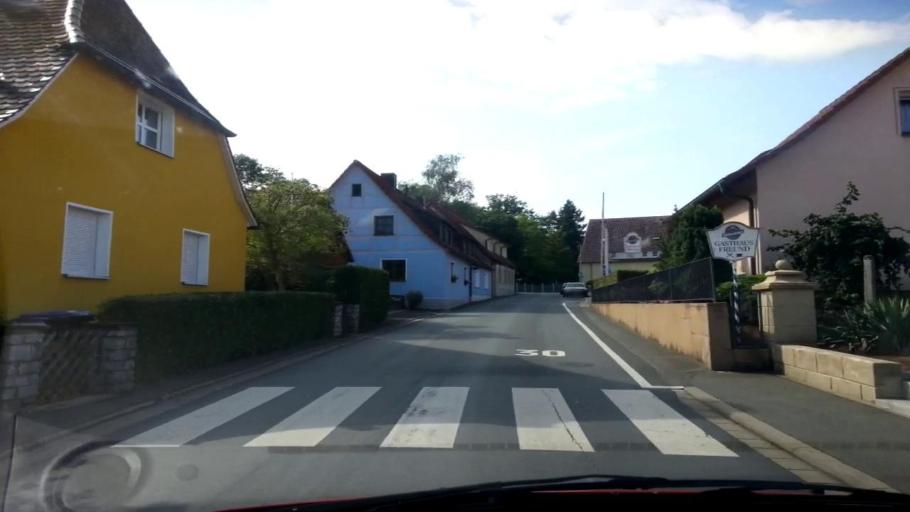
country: DE
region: Bavaria
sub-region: Upper Franconia
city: Heroldsbach
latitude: 49.6894
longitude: 11.0041
